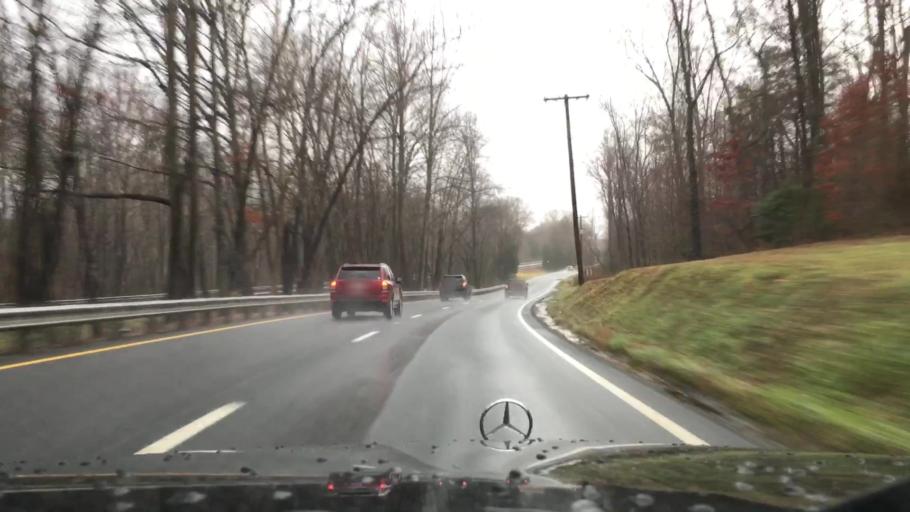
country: US
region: Virginia
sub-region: Albemarle County
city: Crozet
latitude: 37.9253
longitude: -78.6781
